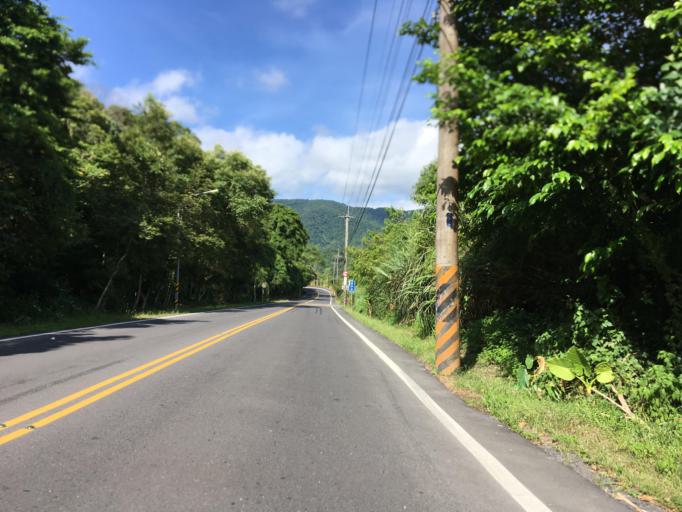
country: TW
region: Taiwan
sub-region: Yilan
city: Yilan
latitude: 24.6148
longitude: 121.6932
